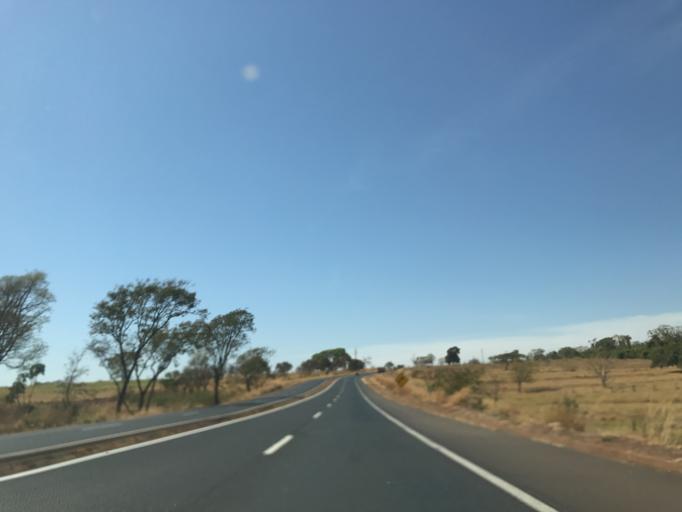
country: BR
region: Minas Gerais
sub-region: Centralina
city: Centralina
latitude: -18.7520
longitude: -49.0821
